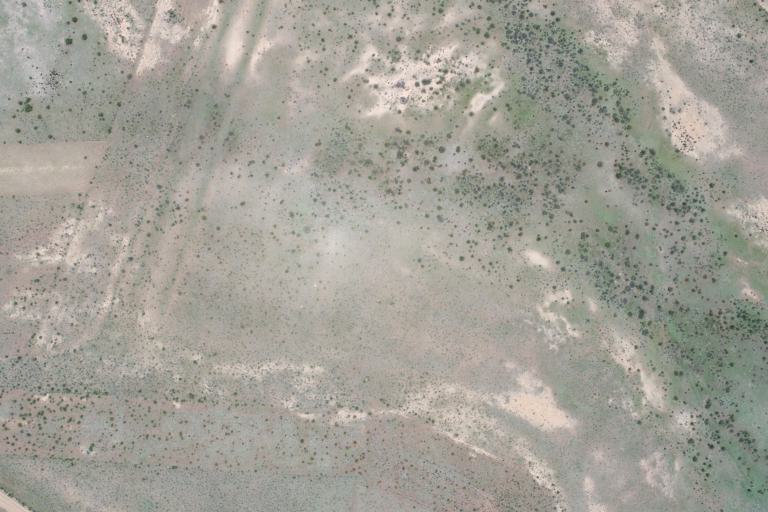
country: BO
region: La Paz
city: Curahuara de Carangas
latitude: -17.2825
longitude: -68.5113
